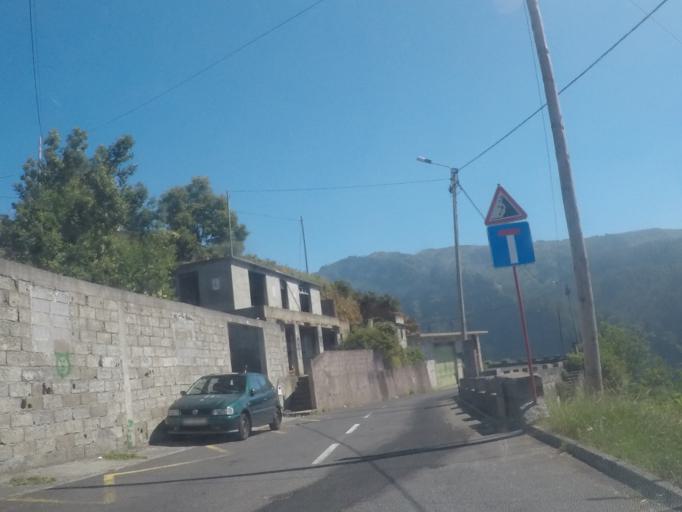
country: PT
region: Madeira
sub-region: Camara de Lobos
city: Curral das Freiras
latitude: 32.6828
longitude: -16.9696
